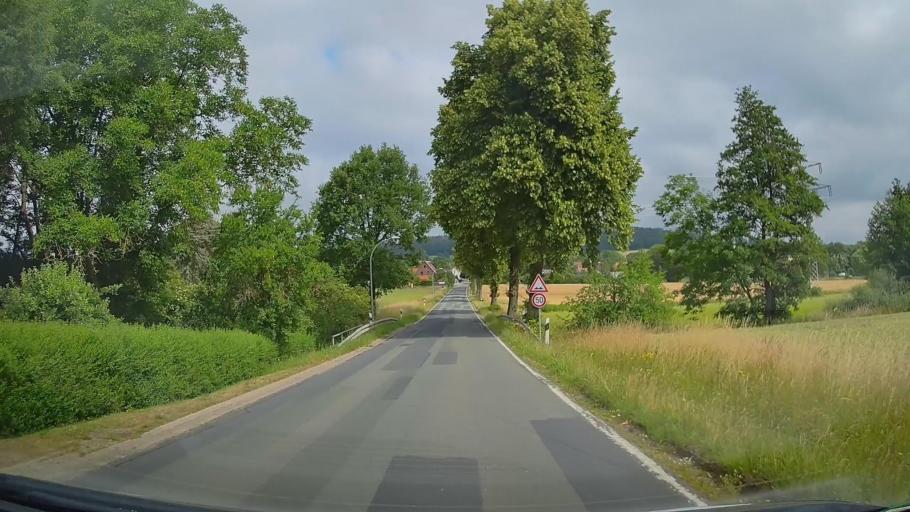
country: DE
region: Lower Saxony
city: Aerzen
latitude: 52.0371
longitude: 9.1982
